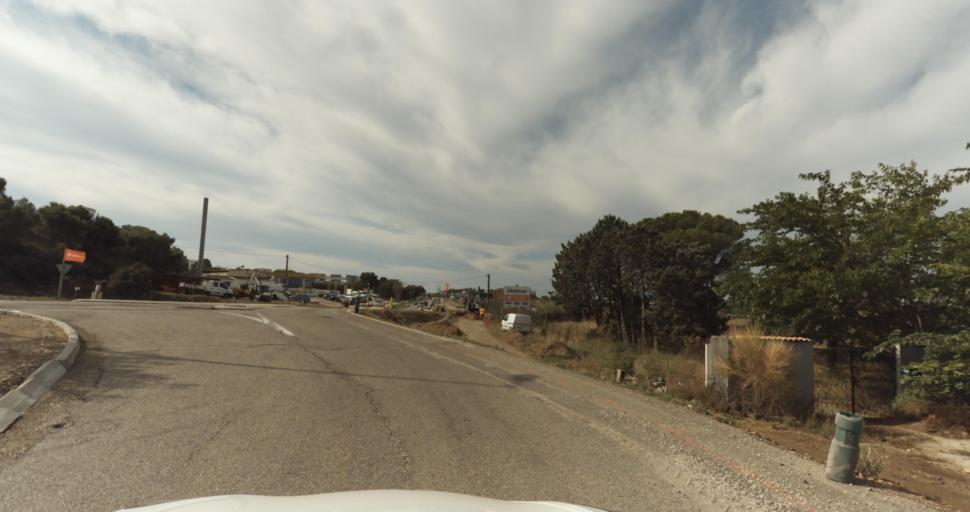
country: FR
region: Provence-Alpes-Cote d'Azur
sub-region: Departement des Bouches-du-Rhone
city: Miramas
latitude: 43.6030
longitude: 5.0071
